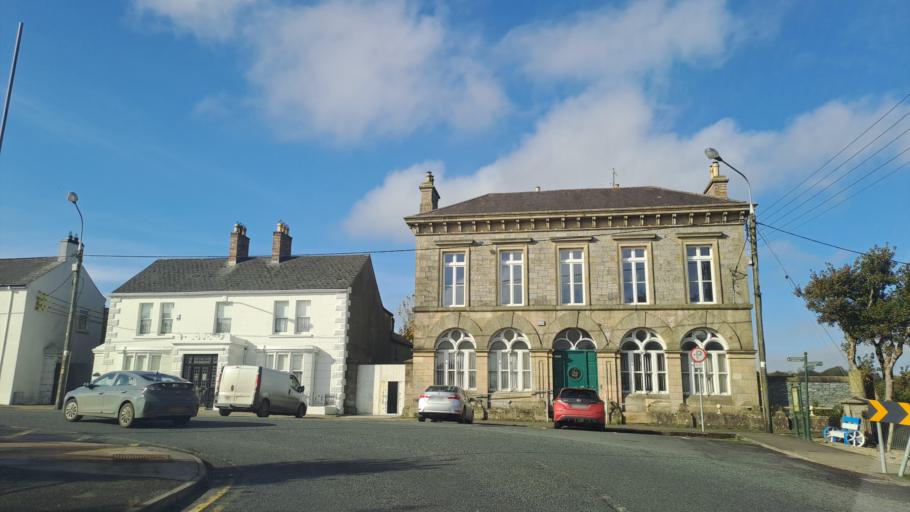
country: IE
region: Ulster
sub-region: An Cabhan
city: Cootehill
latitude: 54.0752
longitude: -7.0792
